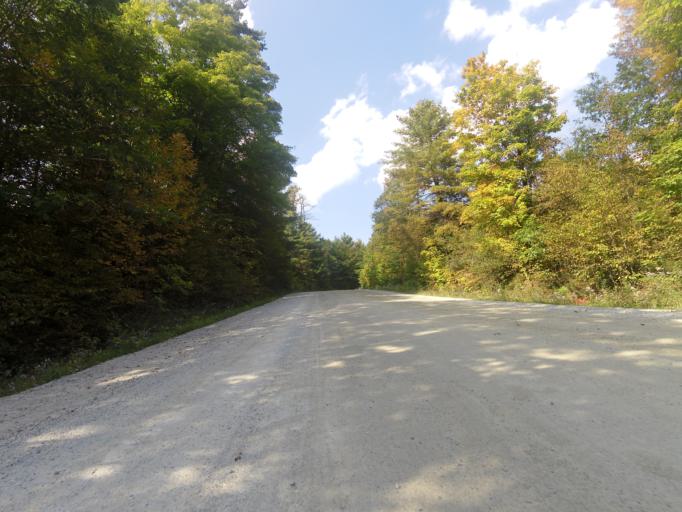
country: CA
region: Ontario
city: Renfrew
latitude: 45.1401
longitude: -76.6684
